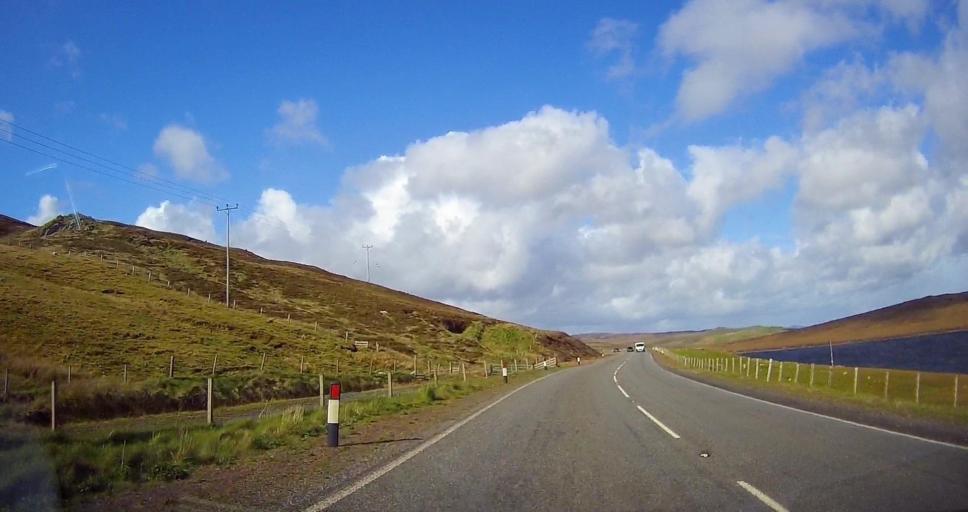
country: GB
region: Scotland
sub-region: Shetland Islands
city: Lerwick
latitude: 60.2562
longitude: -1.2265
